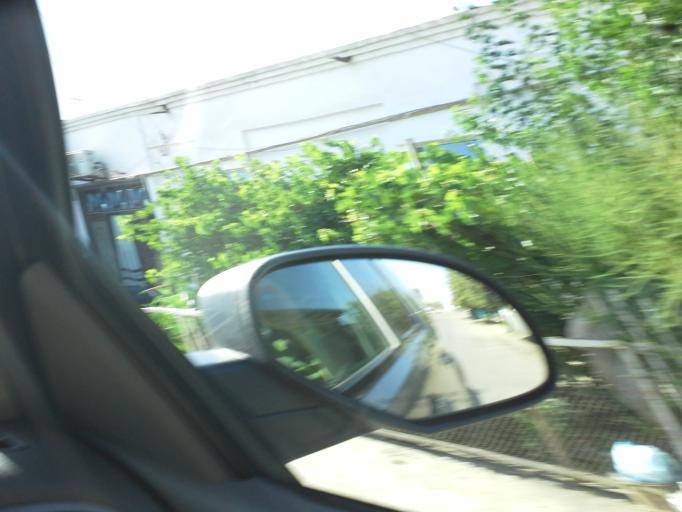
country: TM
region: Dasoguz
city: Dasoguz
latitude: 41.8259
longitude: 59.9786
